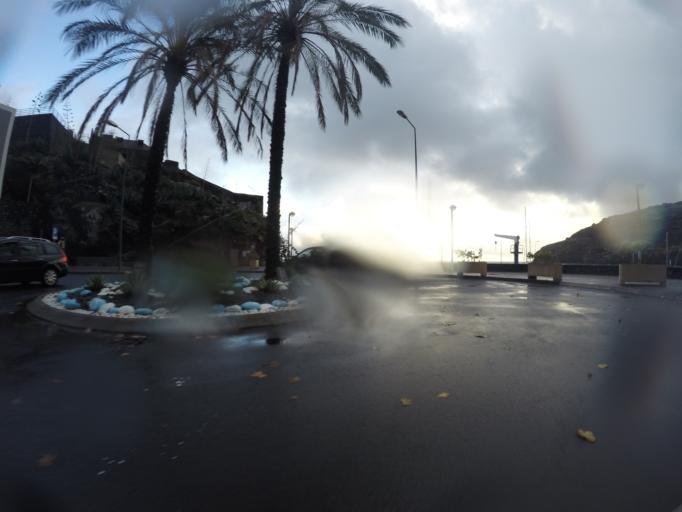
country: PT
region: Madeira
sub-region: Machico
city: Machico
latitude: 32.7186
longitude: -16.7595
